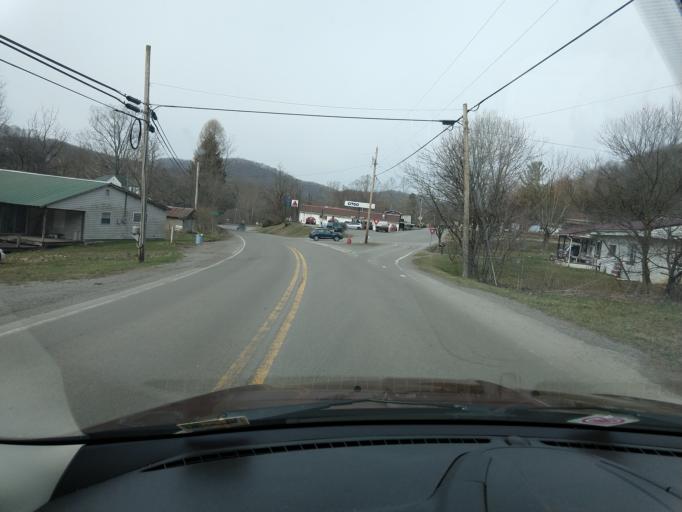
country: US
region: West Virginia
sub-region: Tucker County
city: Parsons
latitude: 39.0952
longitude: -79.6636
